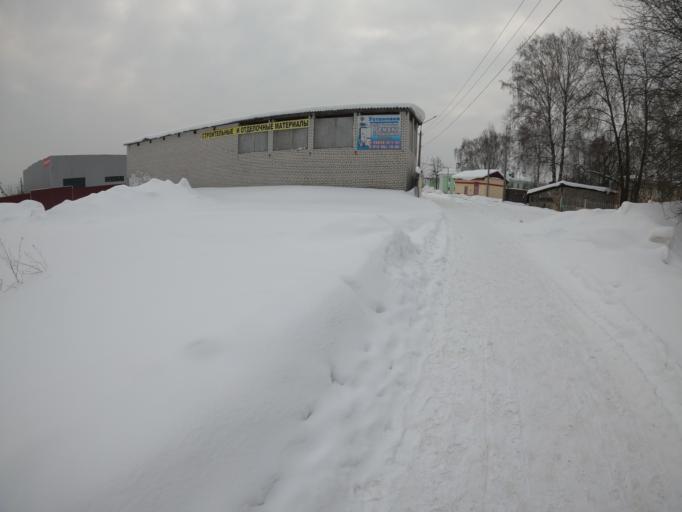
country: RU
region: Moskovskaya
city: Elektrogorsk
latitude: 55.8814
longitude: 38.7876
